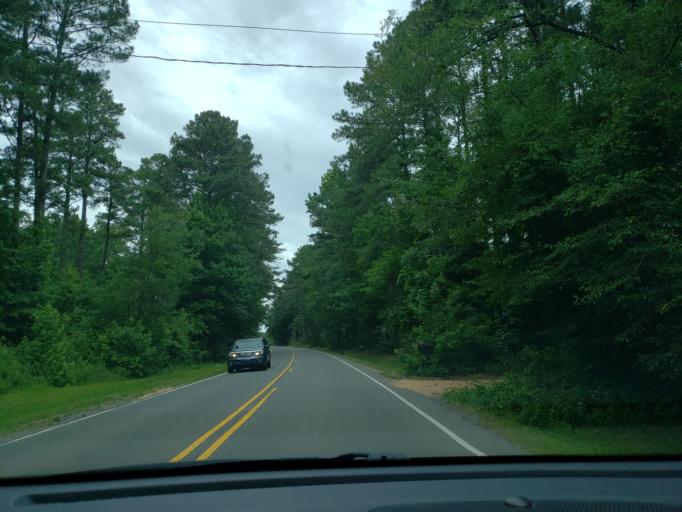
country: US
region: North Carolina
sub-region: Chatham County
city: Fearrington Village
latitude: 35.7800
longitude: -79.0071
